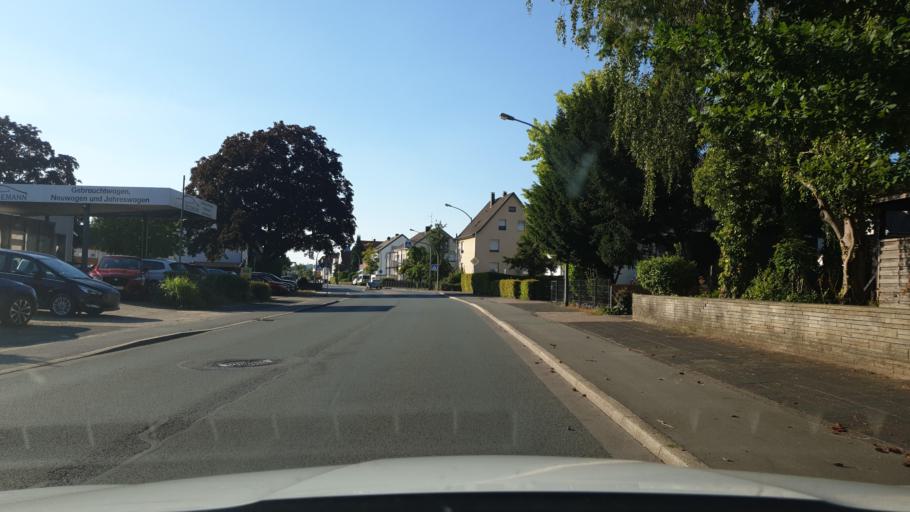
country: DE
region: North Rhine-Westphalia
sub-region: Regierungsbezirk Detmold
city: Bad Salzuflen
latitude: 52.0710
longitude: 8.7670
